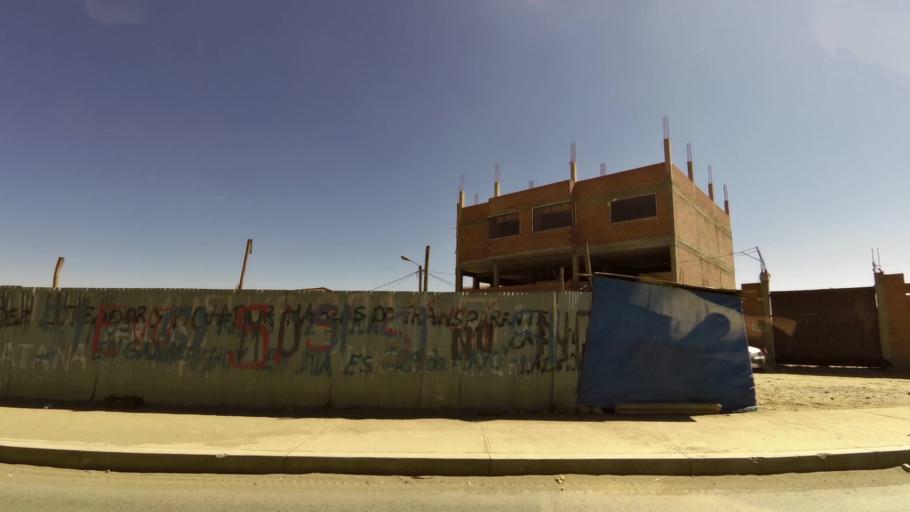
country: BO
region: La Paz
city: La Paz
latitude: -16.5158
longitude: -68.2194
